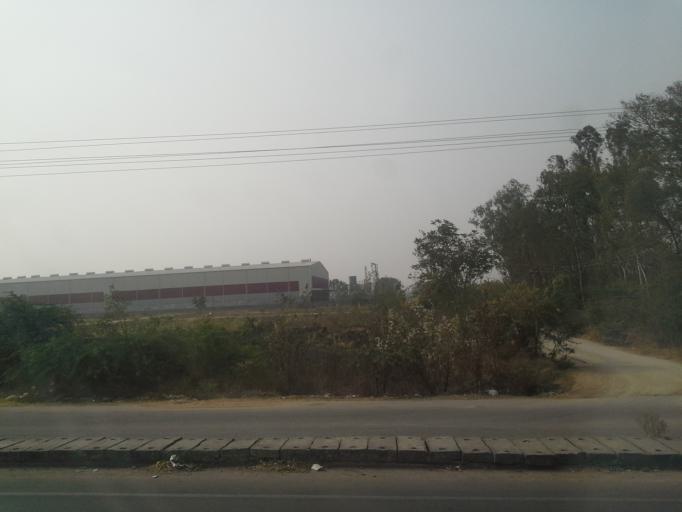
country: IN
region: Telangana
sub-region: Medak
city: Patancheru
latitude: 17.5355
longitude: 78.2464
